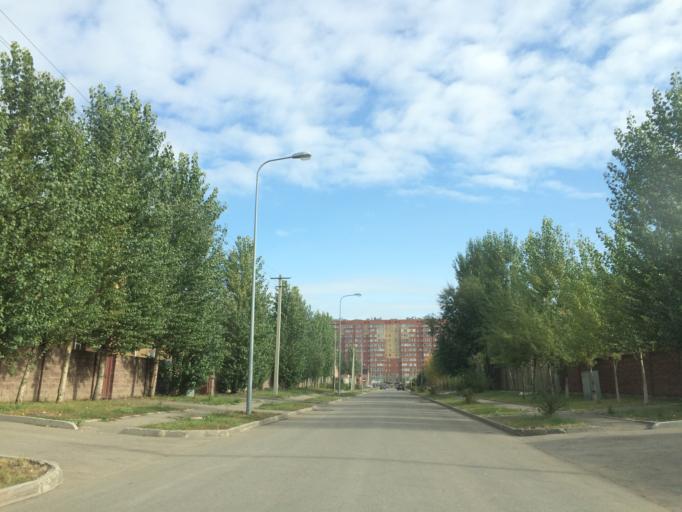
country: KZ
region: Astana Qalasy
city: Astana
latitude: 51.1765
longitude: 71.3713
